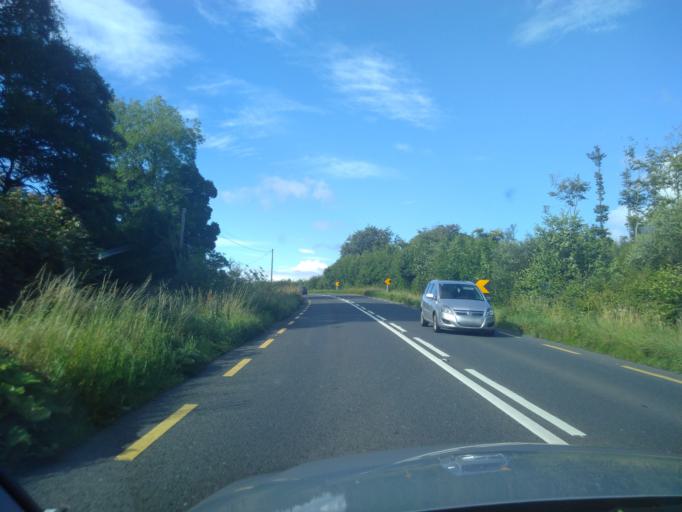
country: IE
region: Ulster
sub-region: County Donegal
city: Ballybofey
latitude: 54.8287
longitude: -7.7481
